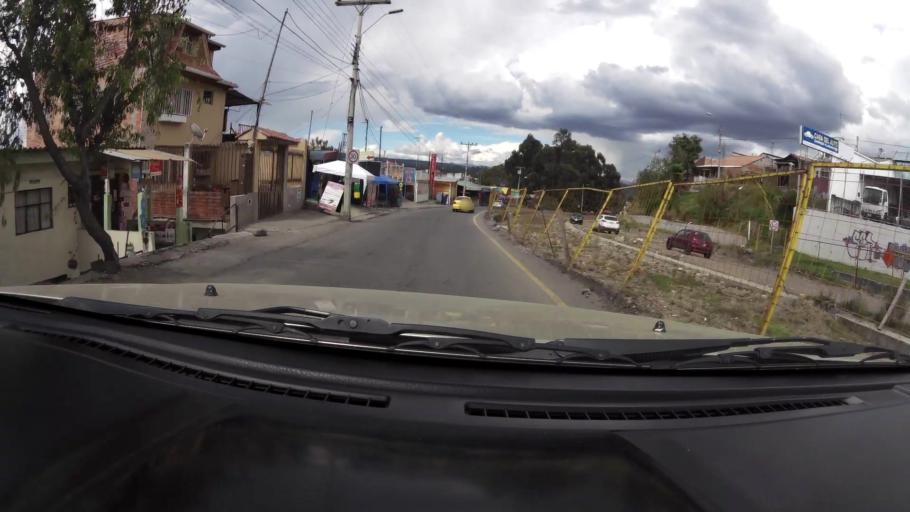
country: EC
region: Azuay
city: Cuenca
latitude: -2.8838
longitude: -78.9808
